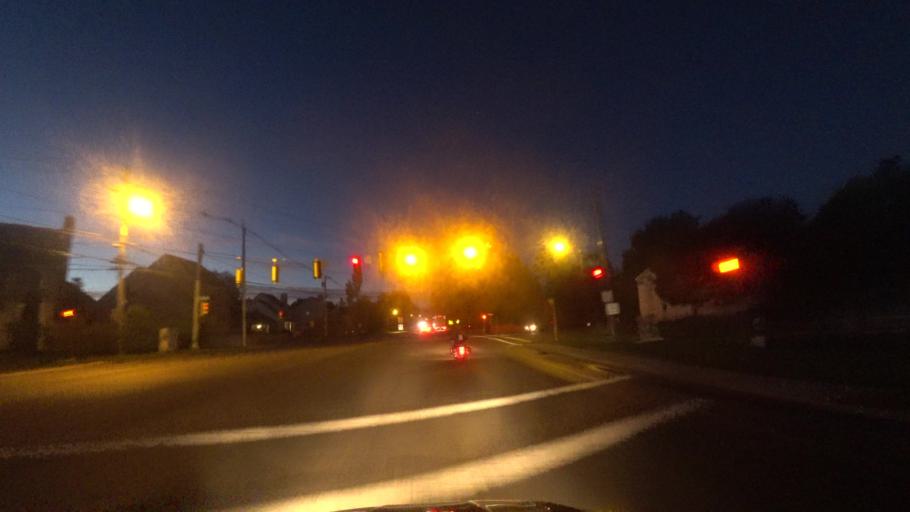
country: US
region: Massachusetts
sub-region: Essex County
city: Andover
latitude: 42.6638
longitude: -71.1173
